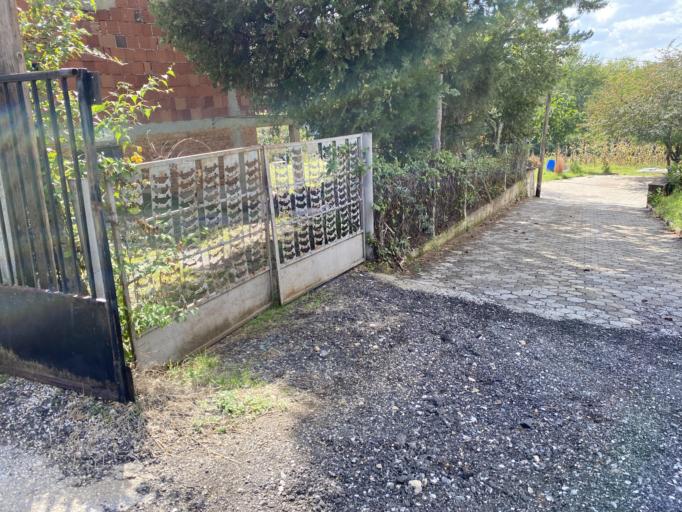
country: MK
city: Radishani
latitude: 42.1022
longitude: 21.4565
